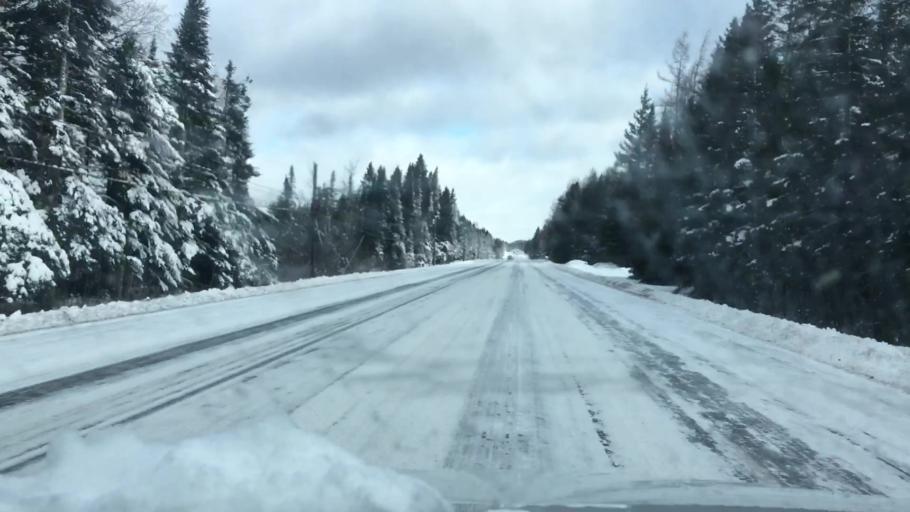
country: US
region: Maine
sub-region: Aroostook County
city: Madawaska
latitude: 47.0156
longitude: -68.0169
